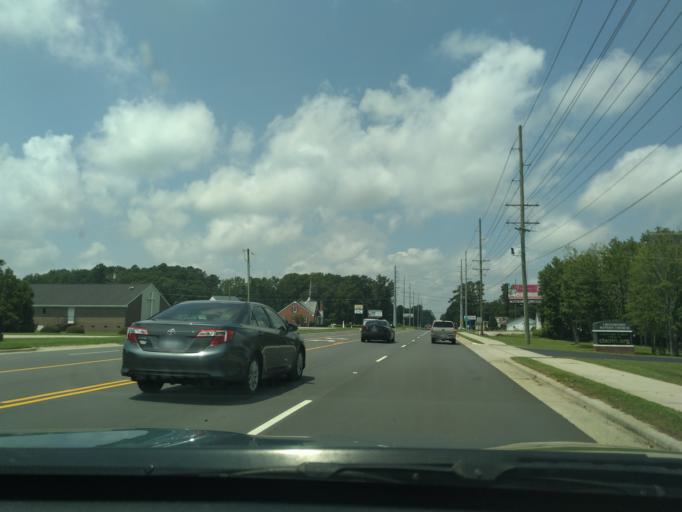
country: US
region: North Carolina
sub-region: Nash County
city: Rocky Mount
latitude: 35.9976
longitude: -77.8332
